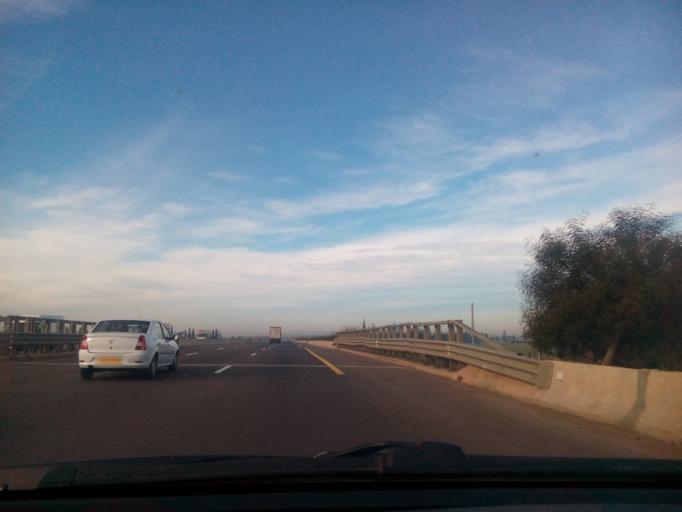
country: DZ
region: Mascara
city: Sig
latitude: 35.6172
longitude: 0.0239
